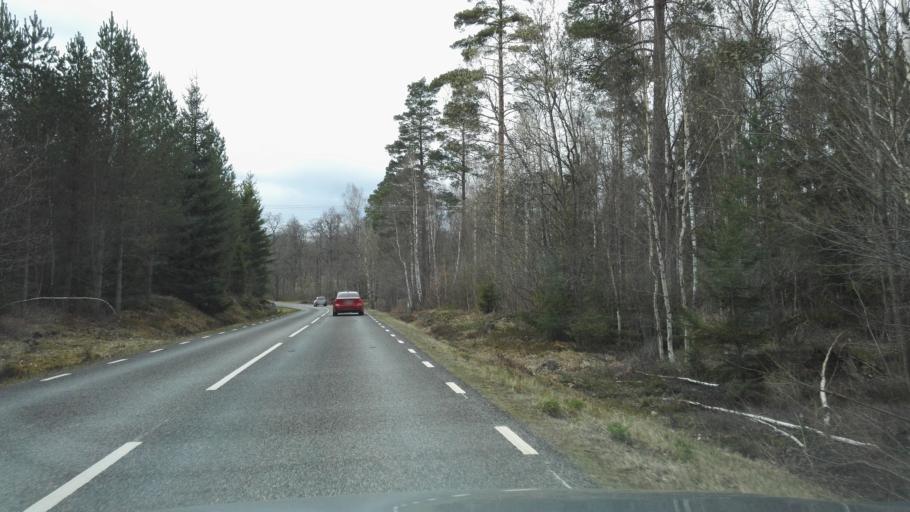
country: SE
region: Kronoberg
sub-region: Vaxjo Kommun
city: Braas
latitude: 57.0618
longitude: 15.0322
